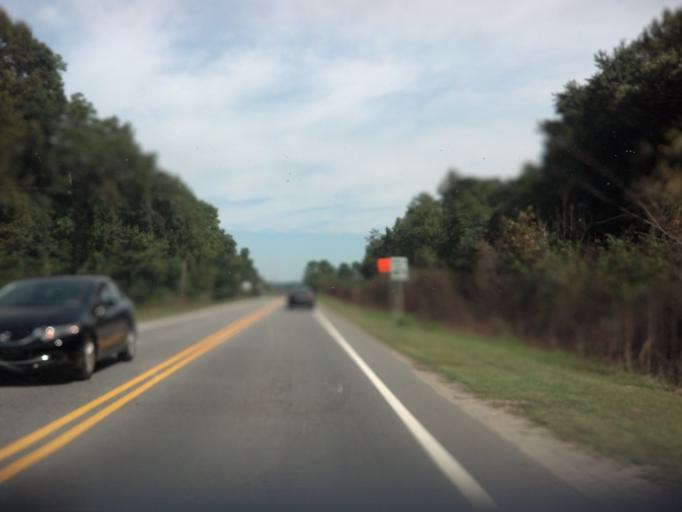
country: US
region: North Carolina
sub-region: Greene County
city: Snow Hill
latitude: 35.4574
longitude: -77.6699
